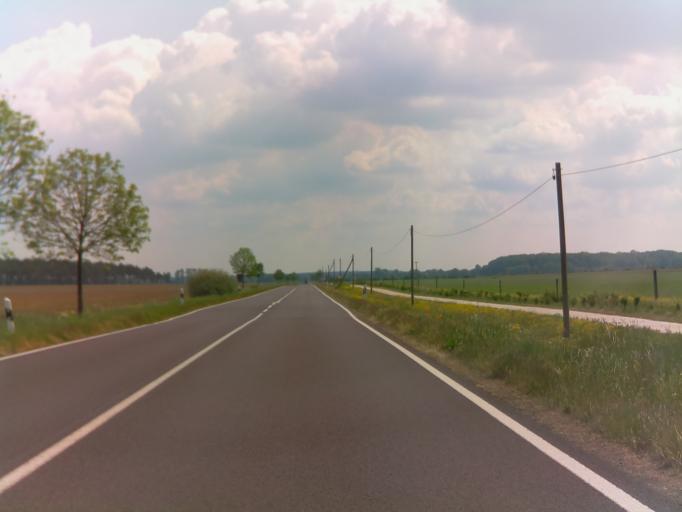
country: DE
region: Saxony-Anhalt
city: Schonhausen
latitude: 52.5519
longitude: 12.0835
